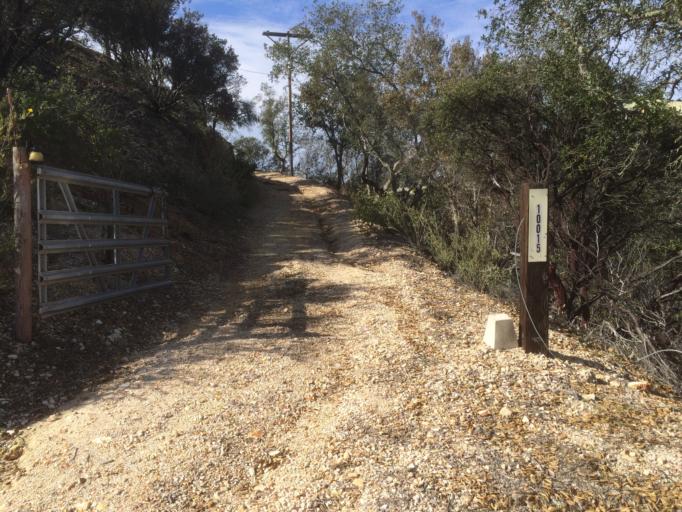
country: US
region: California
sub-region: San Luis Obispo County
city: Nipomo
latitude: 35.0553
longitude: -120.4019
